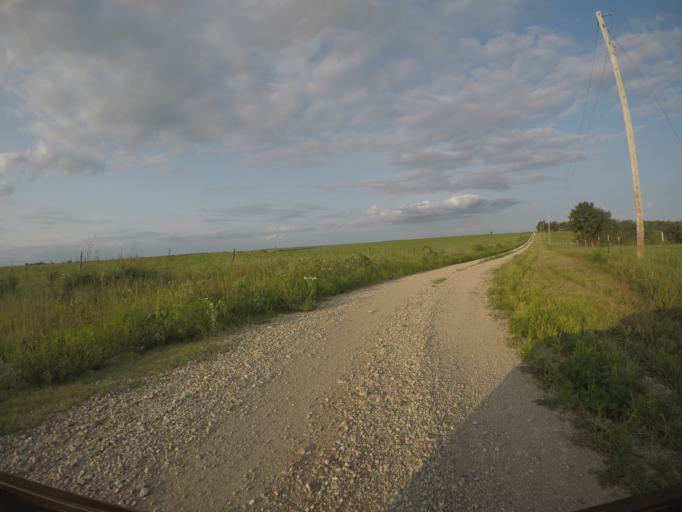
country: US
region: Kansas
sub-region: Wabaunsee County
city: Alma
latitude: 39.0797
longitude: -96.3772
